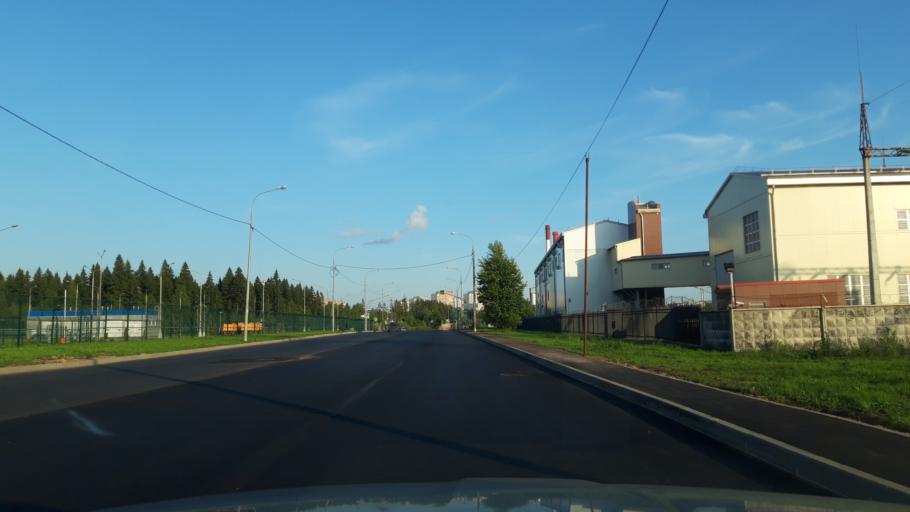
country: RU
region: Moskovskaya
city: Alabushevo
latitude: 55.9991
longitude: 37.1569
